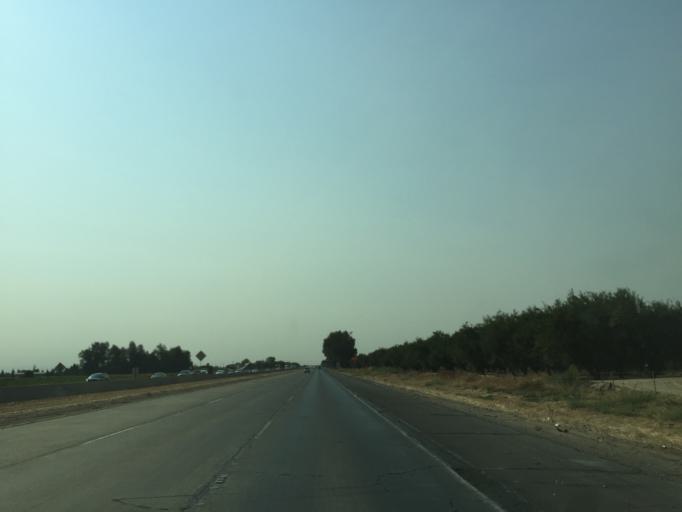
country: US
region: California
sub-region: Merced County
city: Delhi
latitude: 37.4600
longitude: -120.8135
